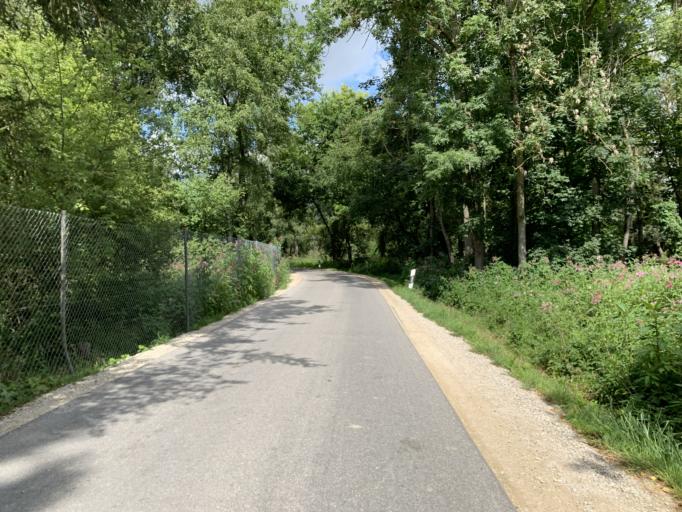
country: DE
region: Bavaria
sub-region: Upper Bavaria
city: Zolling
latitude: 48.4430
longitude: 11.7897
